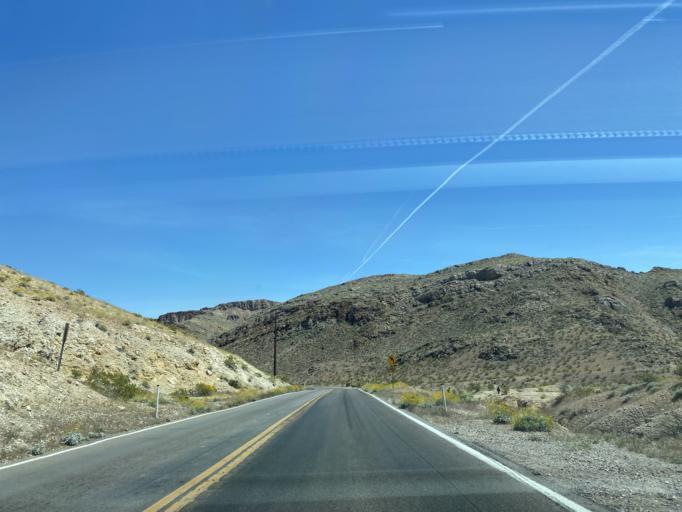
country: US
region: Nevada
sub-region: Clark County
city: Nellis Air Force Base
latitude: 36.2022
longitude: -114.9855
